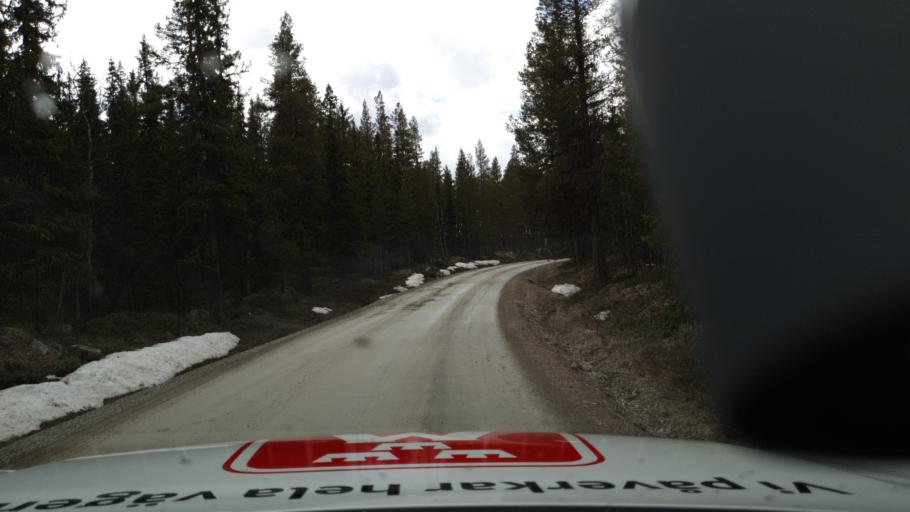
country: SE
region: Jaemtland
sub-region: Bergs Kommun
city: Hoverberg
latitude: 62.7694
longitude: 13.8294
